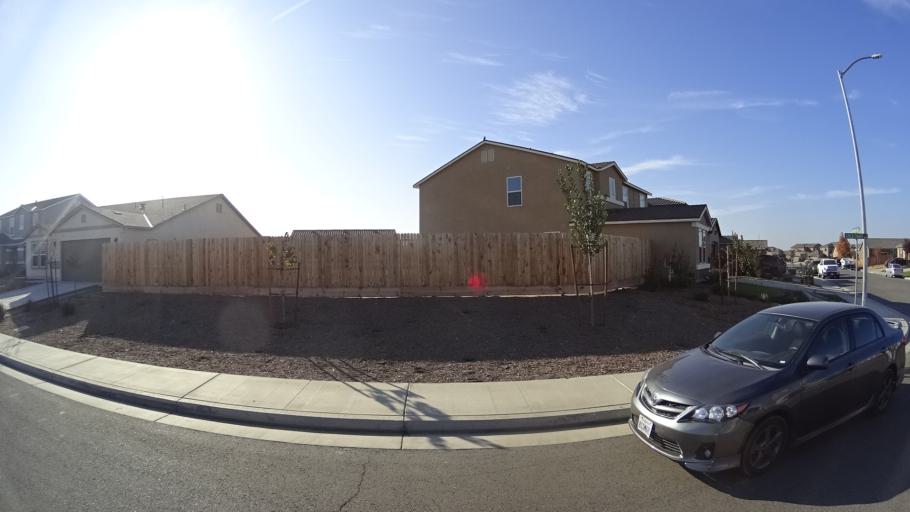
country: US
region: California
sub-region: Kern County
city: Greenfield
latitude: 35.2809
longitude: -119.0666
